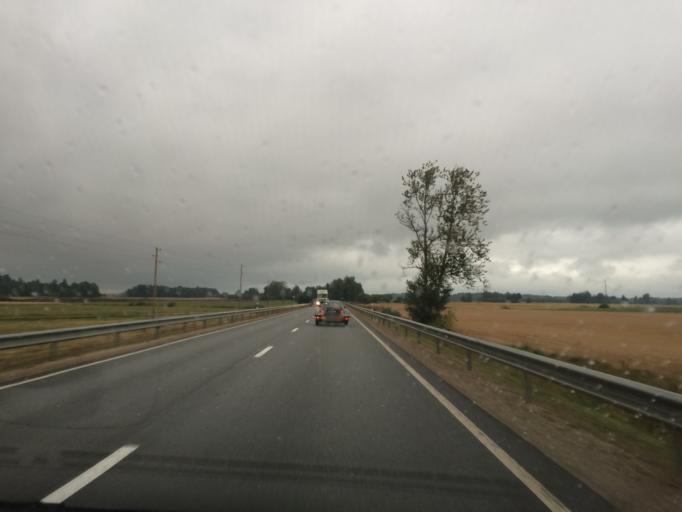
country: LV
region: Livani
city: Livani
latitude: 56.5344
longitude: 26.3152
